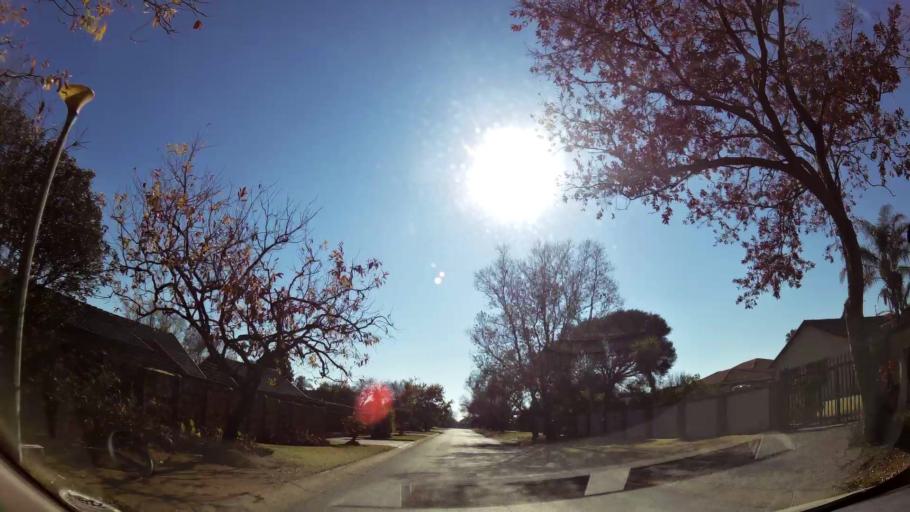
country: ZA
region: Mpumalanga
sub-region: Nkangala District Municipality
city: Witbank
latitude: -25.8906
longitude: 29.2536
